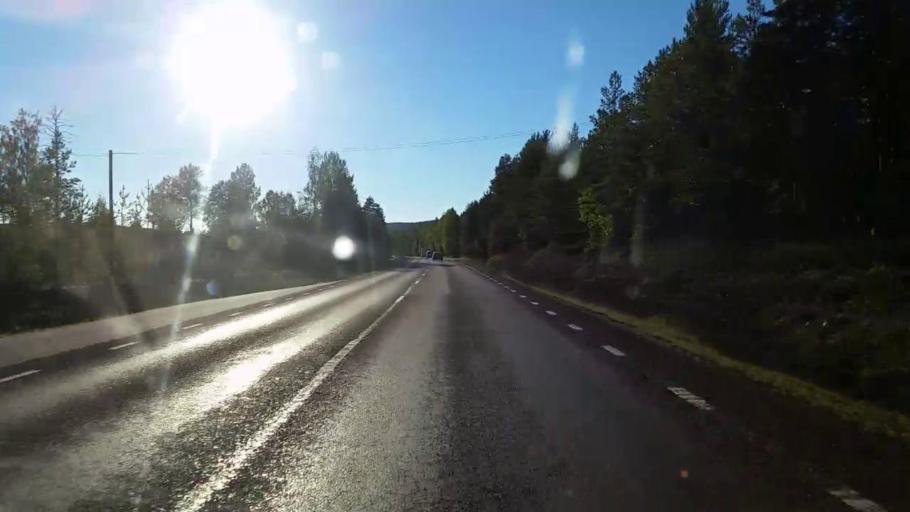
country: SE
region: Gaevleborg
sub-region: Hudiksvalls Kommun
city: Delsbo
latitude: 61.8069
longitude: 16.4105
